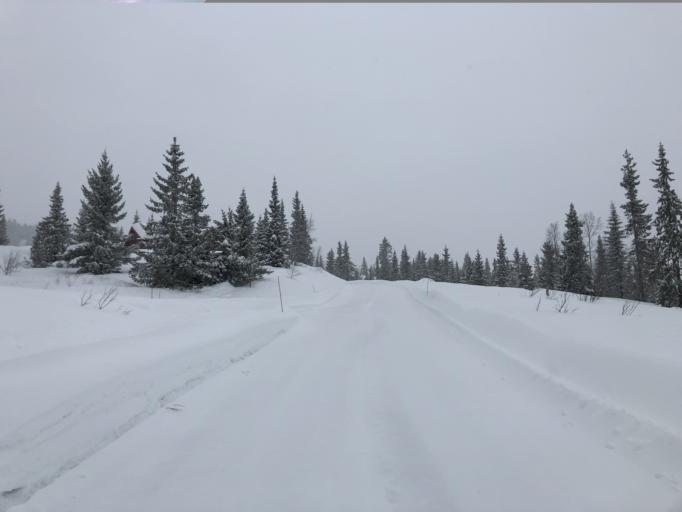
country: NO
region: Oppland
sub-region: Gausdal
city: Segalstad bru
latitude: 61.3276
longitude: 10.0560
